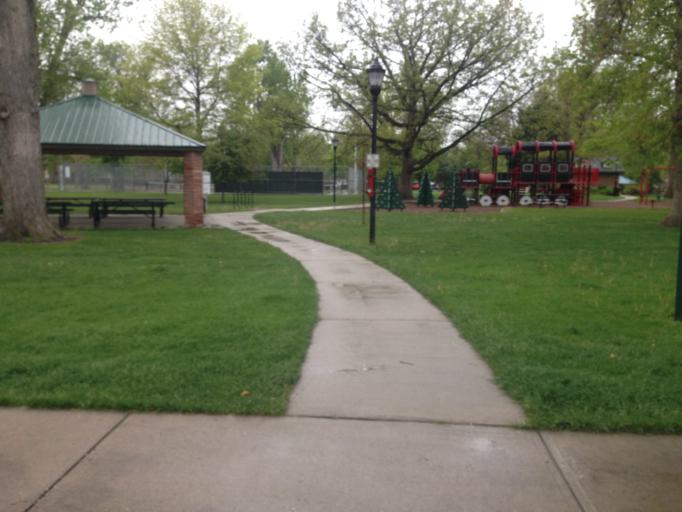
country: US
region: Colorado
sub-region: Boulder County
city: Longmont
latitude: 40.1706
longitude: -105.0972
